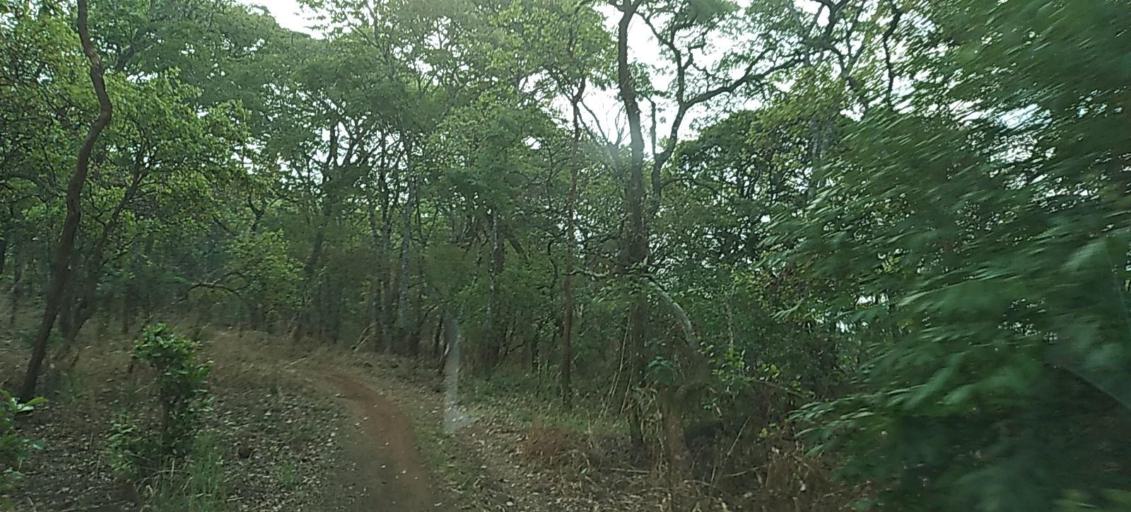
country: ZM
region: North-Western
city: Solwezi
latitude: -12.0448
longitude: 26.0166
